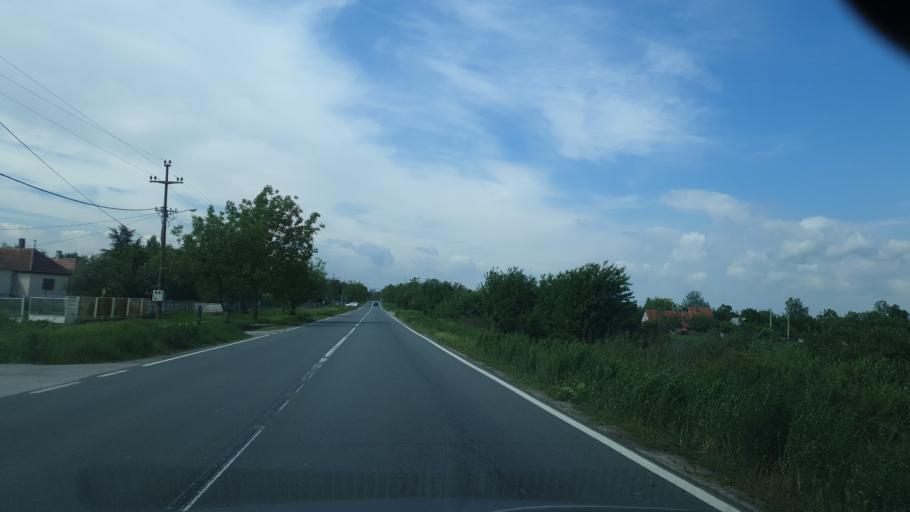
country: RS
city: Stubline
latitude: 44.5848
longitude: 20.1505
